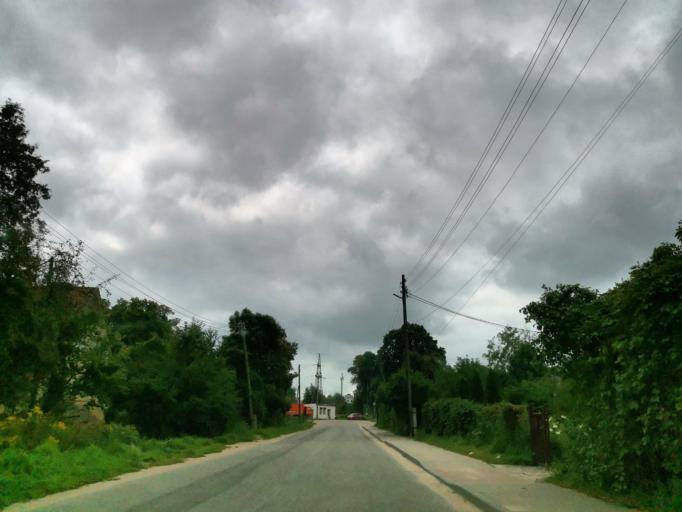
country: RU
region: Kaliningrad
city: Chernyakhovsk
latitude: 54.6520
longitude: 21.8341
